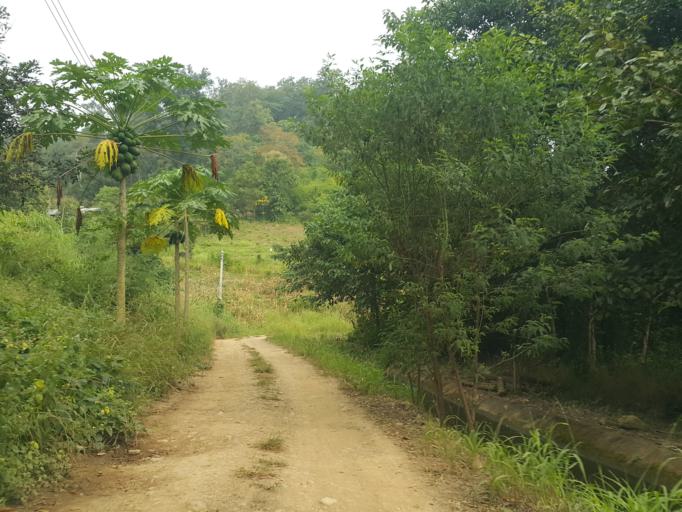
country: TH
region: Mae Hong Son
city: Wiang Nuea
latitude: 19.3871
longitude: 98.4665
